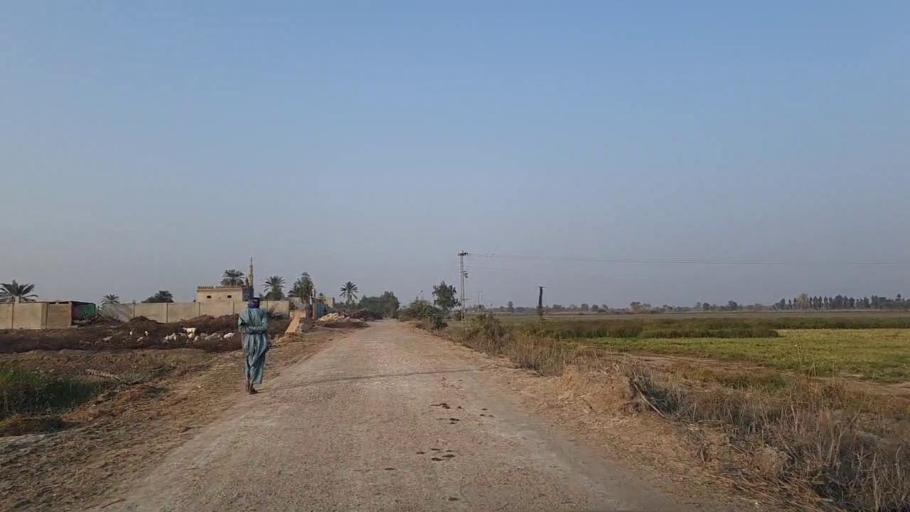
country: PK
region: Sindh
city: Daur
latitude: 26.4235
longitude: 68.3935
